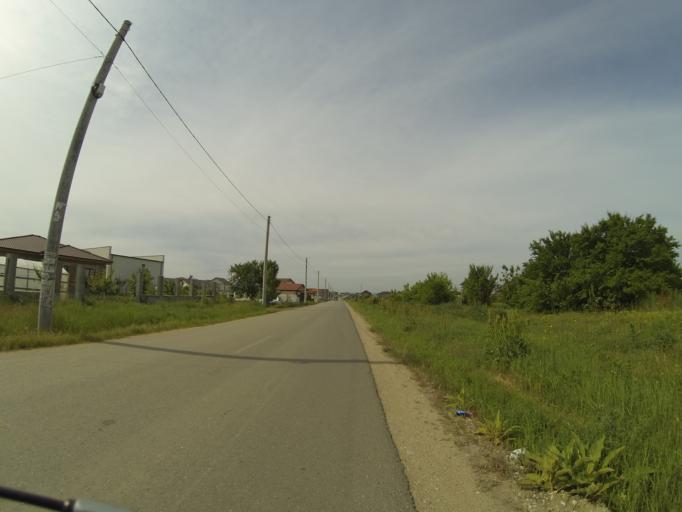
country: RO
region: Dolj
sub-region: Comuna Malu Mare
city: Preajba
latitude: 44.2868
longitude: 23.8483
